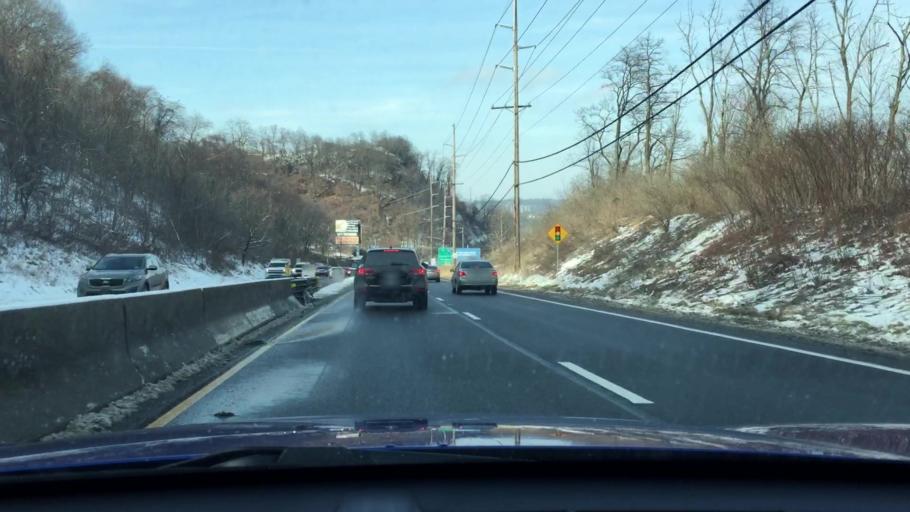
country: US
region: Pennsylvania
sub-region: Allegheny County
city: Braddock
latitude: 40.3996
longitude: -79.8782
